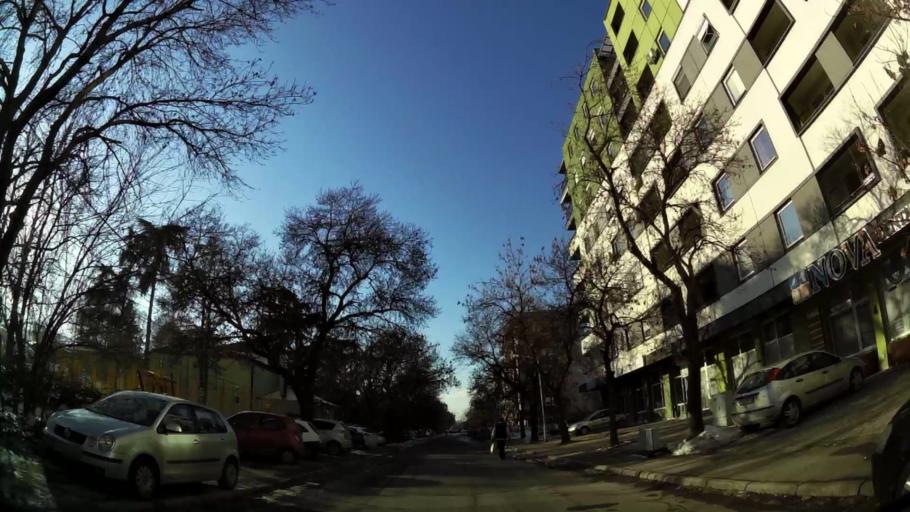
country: MK
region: Karpos
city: Skopje
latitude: 42.0001
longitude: 21.4030
